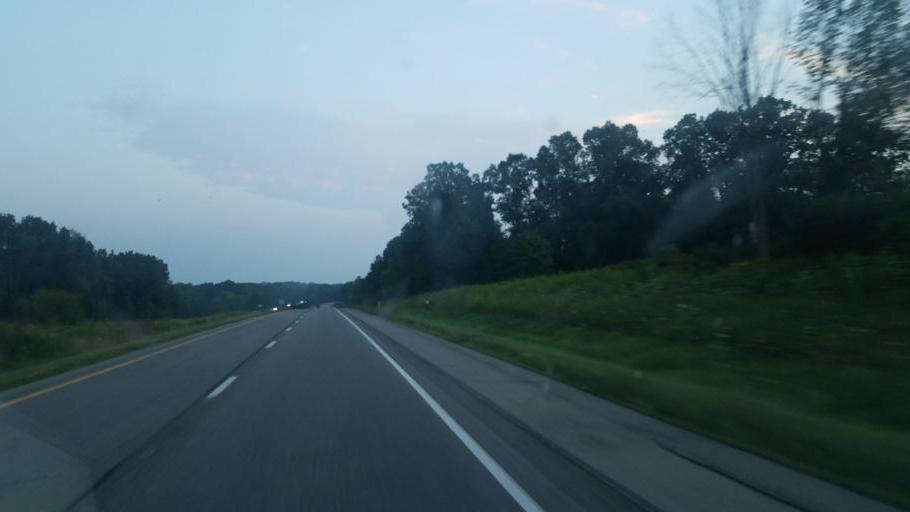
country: US
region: Pennsylvania
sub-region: Mercer County
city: Stoneboro
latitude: 41.4108
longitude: -80.1583
